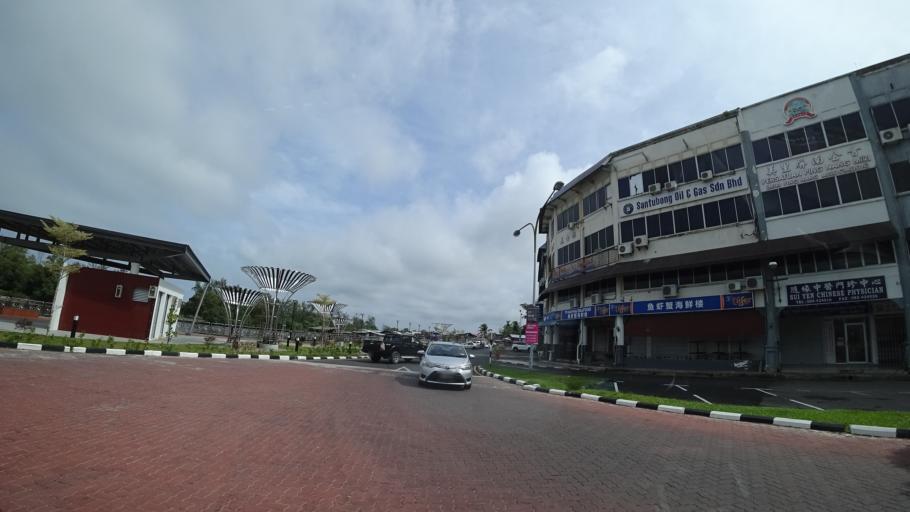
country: MY
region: Sarawak
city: Miri
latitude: 4.3992
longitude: 113.9863
